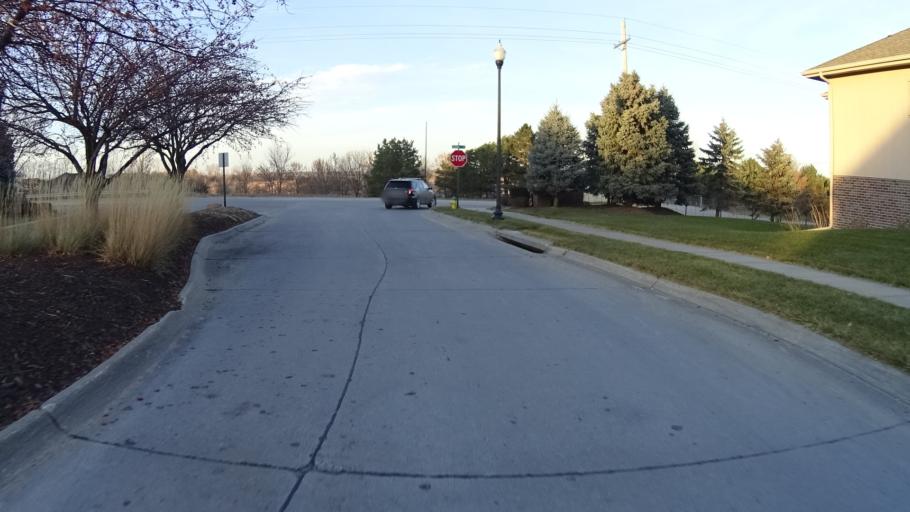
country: US
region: Nebraska
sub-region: Sarpy County
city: Papillion
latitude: 41.1323
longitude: -96.0688
